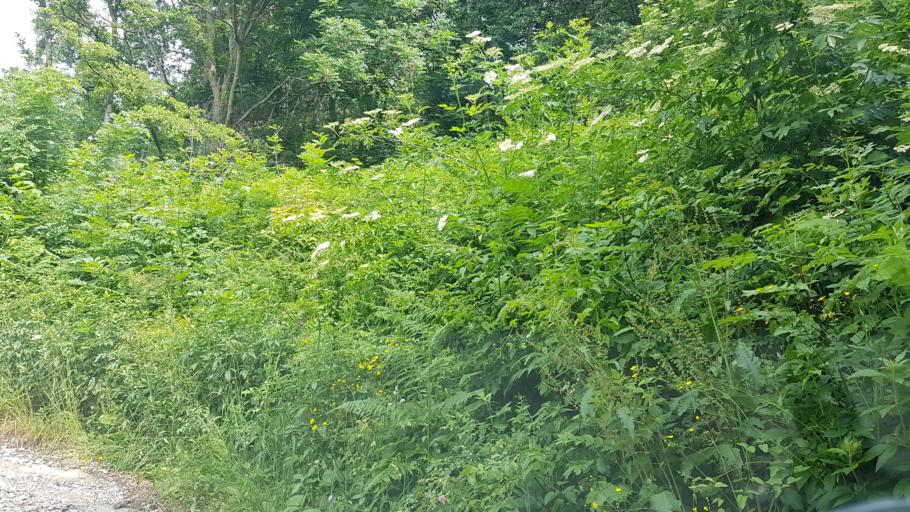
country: IT
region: Friuli Venezia Giulia
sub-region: Provincia di Udine
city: Pulfero
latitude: 46.1765
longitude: 13.4396
